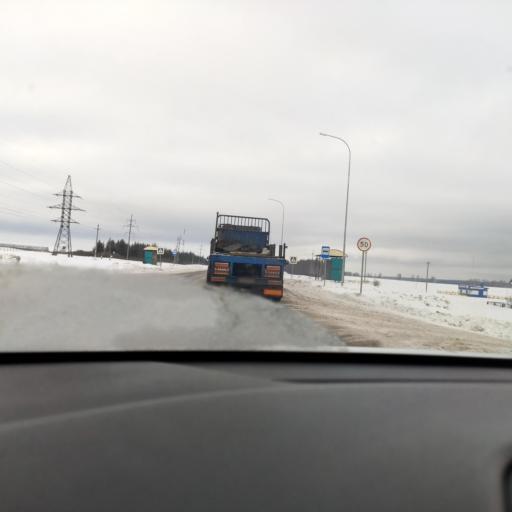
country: RU
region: Tatarstan
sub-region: Arskiy Rayon
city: Arsk
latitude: 56.1977
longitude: 49.9574
